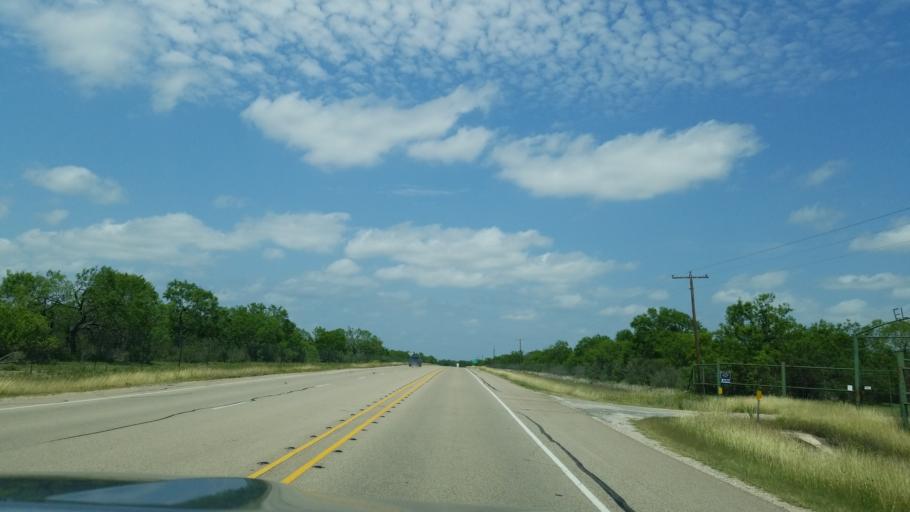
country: US
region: Texas
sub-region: Frio County
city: Pearsall
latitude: 29.0080
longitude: -99.1971
